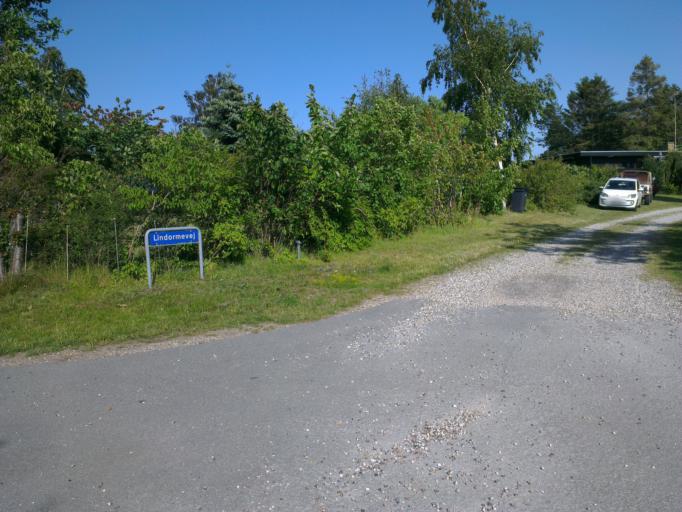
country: DK
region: Capital Region
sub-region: Halsnaes Kommune
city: Hundested
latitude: 55.9299
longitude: 11.9181
